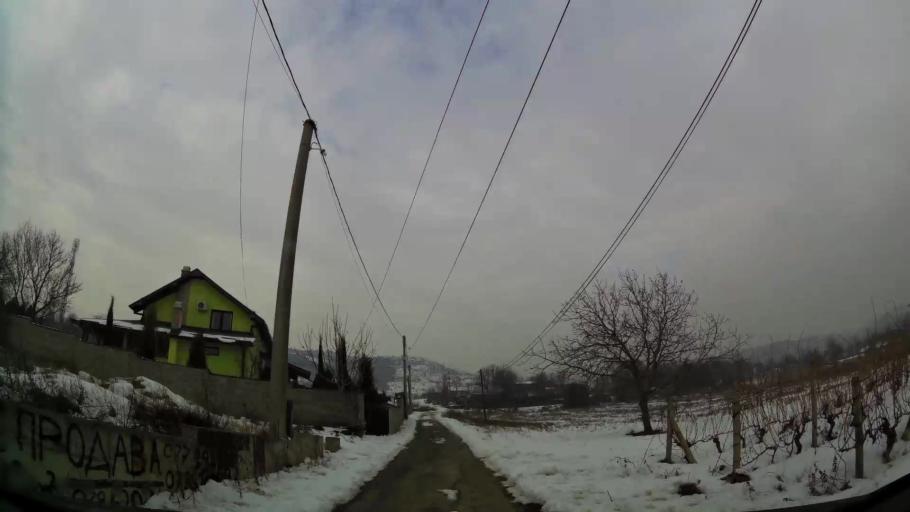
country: MK
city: Kondovo
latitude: 42.0462
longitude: 21.3400
